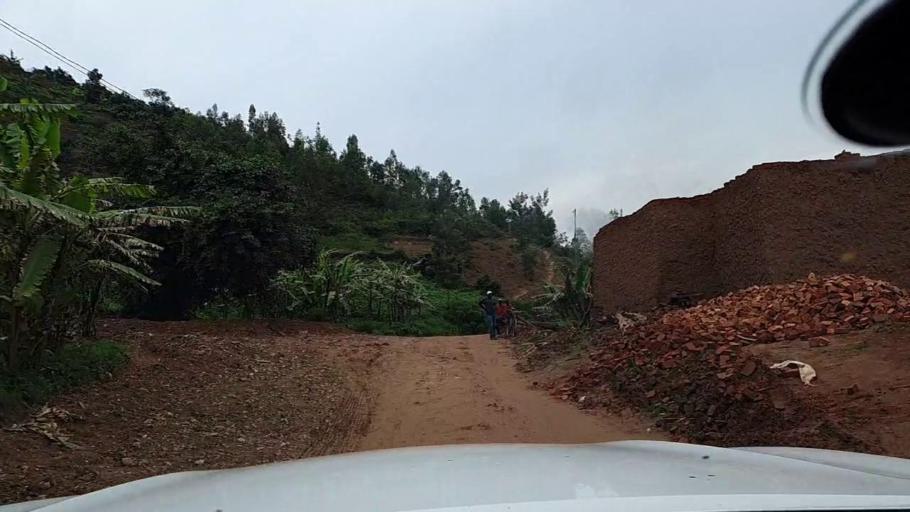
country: RW
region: Kigali
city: Kigali
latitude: -1.9522
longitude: 29.9910
